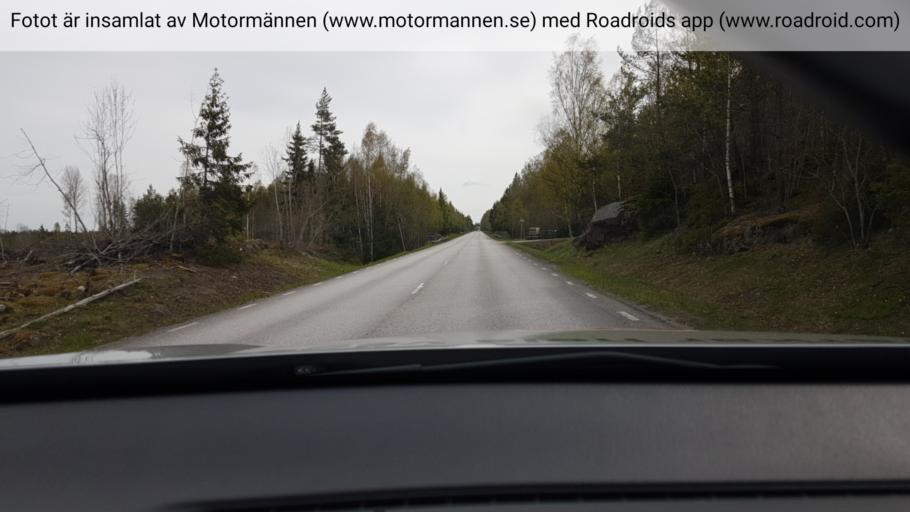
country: SE
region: Stockholm
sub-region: Norrtalje Kommun
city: Nykvarn
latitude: 59.8197
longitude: 18.0448
